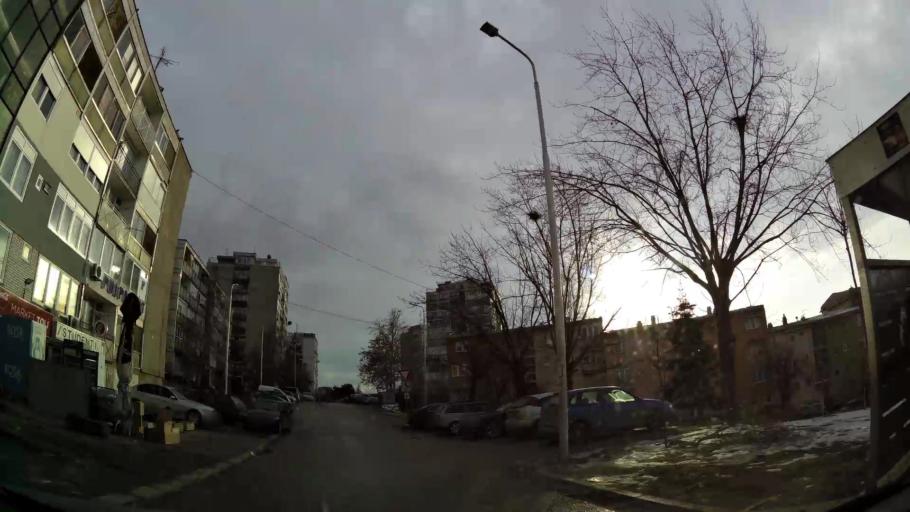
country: XK
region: Pristina
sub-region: Komuna e Prishtines
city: Pristina
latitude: 42.6526
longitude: 21.1629
